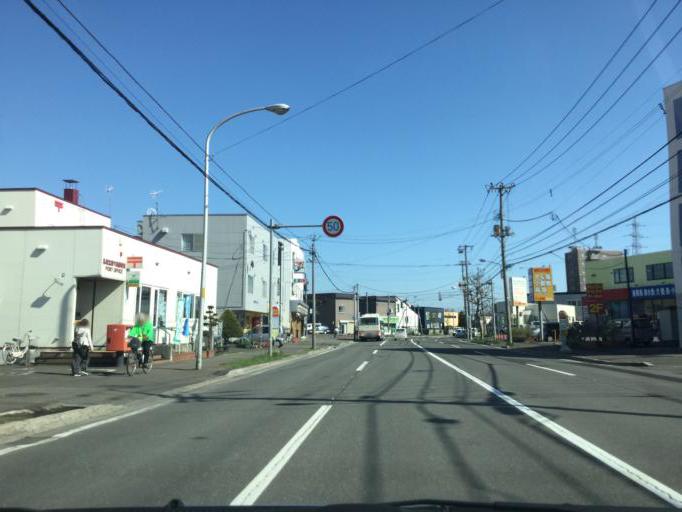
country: JP
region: Hokkaido
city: Sapporo
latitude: 43.0197
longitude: 141.4344
